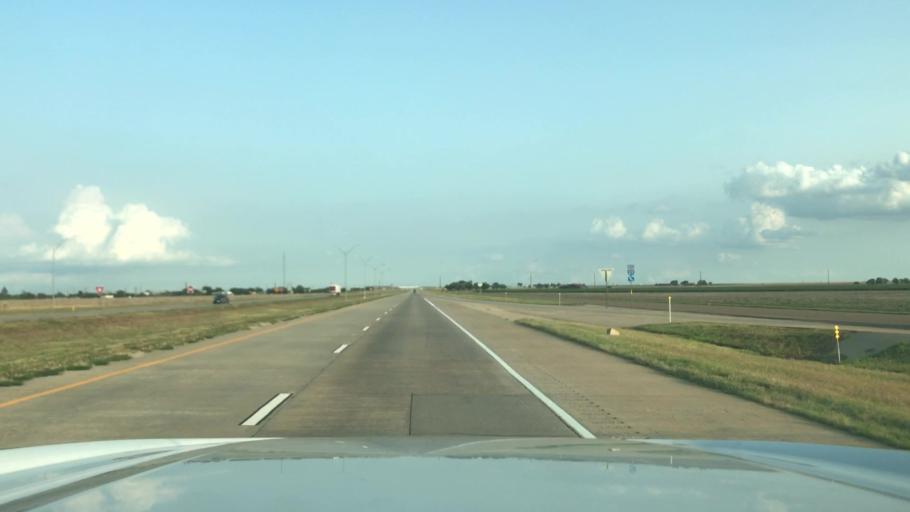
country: US
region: Texas
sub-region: Swisher County
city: Tulia
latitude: 34.3684
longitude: -101.7662
